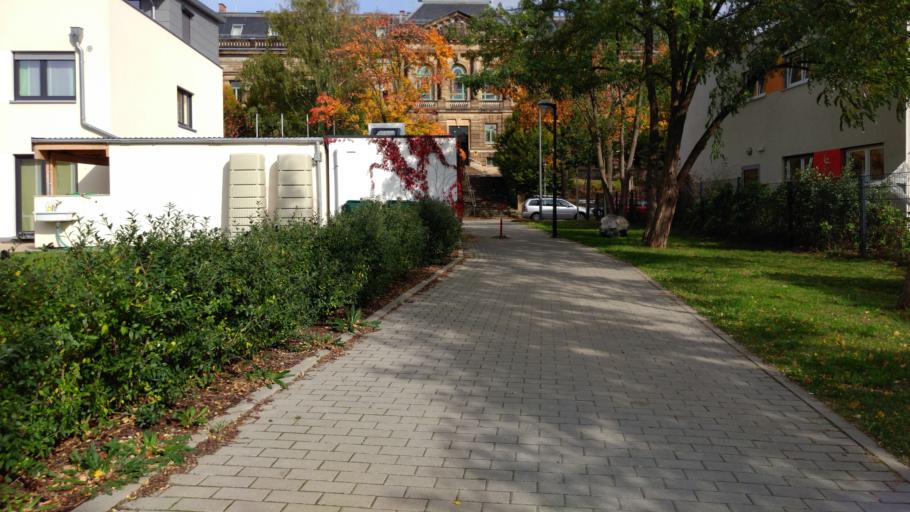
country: DE
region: Saxony
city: Albertstadt
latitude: 51.0824
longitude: 13.7530
